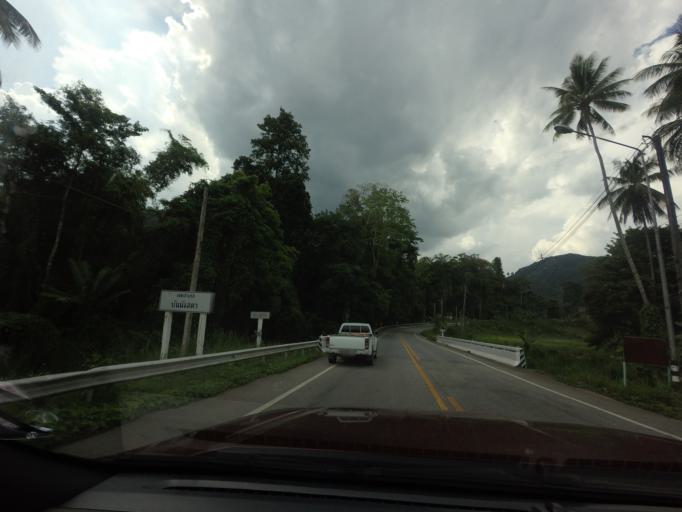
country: TH
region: Yala
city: Than To
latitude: 6.1979
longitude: 101.1734
